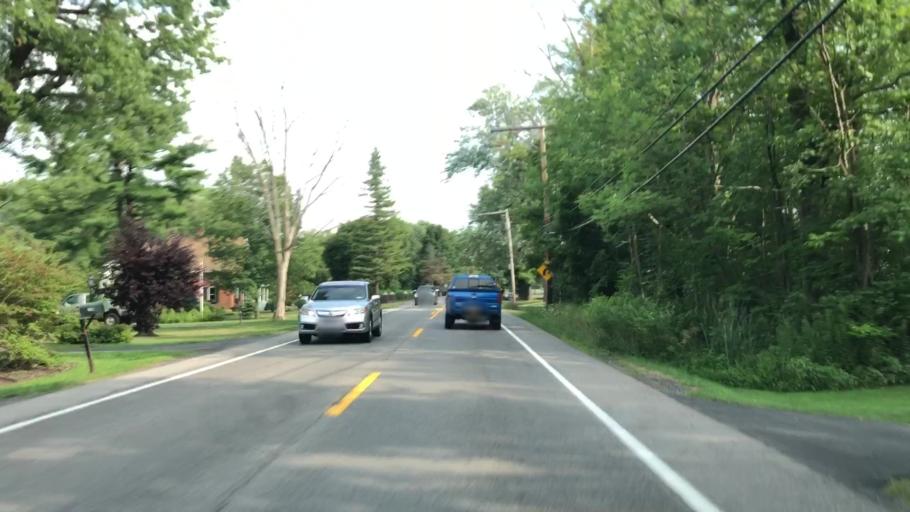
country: US
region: New York
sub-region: Erie County
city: Elma Center
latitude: 42.8419
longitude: -78.6379
